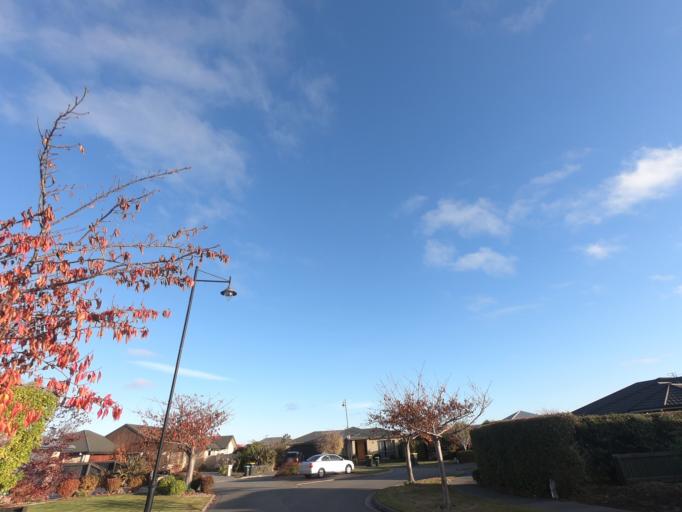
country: NZ
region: Canterbury
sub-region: Selwyn District
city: Prebbleton
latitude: -43.5666
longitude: 172.5688
